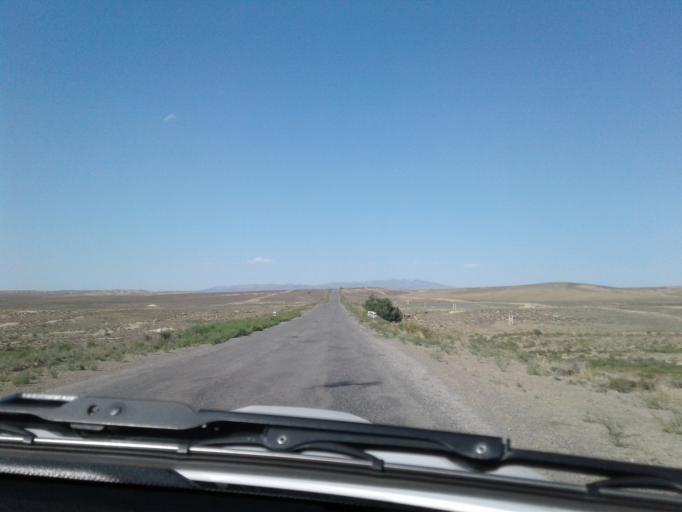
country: TM
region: Balkan
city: Magtymguly
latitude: 38.6303
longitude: 56.2410
